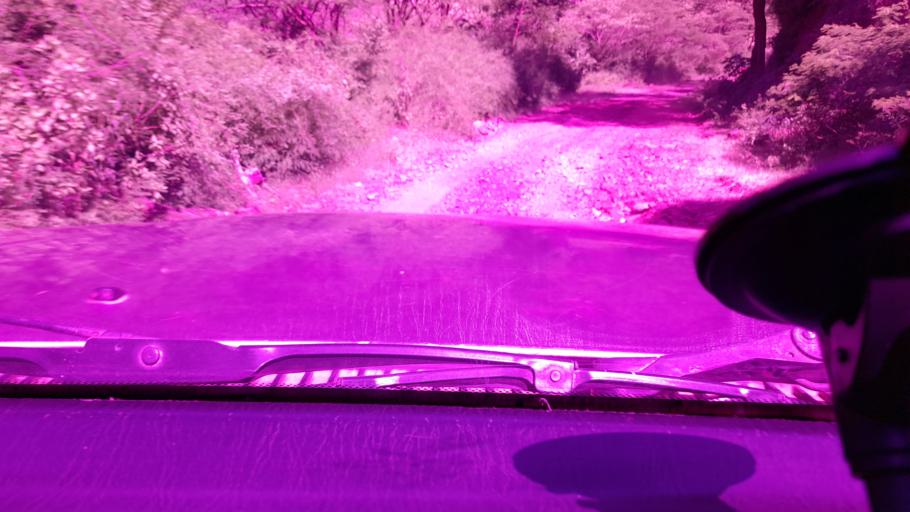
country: ET
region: Oromiya
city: Jima
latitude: 7.8012
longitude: 37.5243
